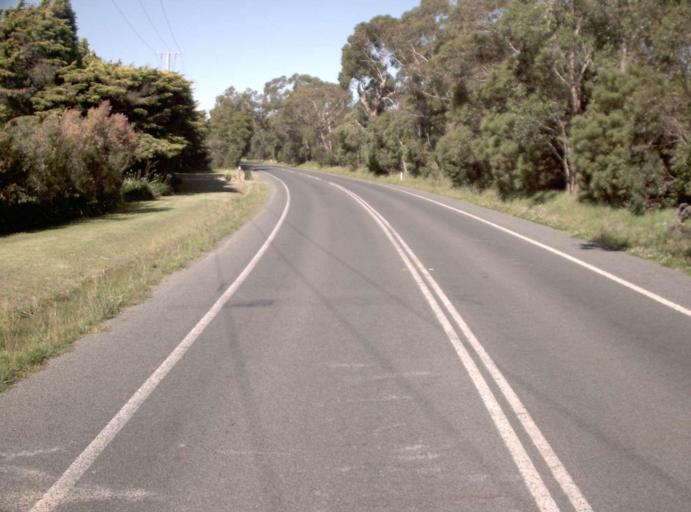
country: AU
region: Victoria
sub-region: Latrobe
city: Morwell
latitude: -38.6685
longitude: 146.4019
